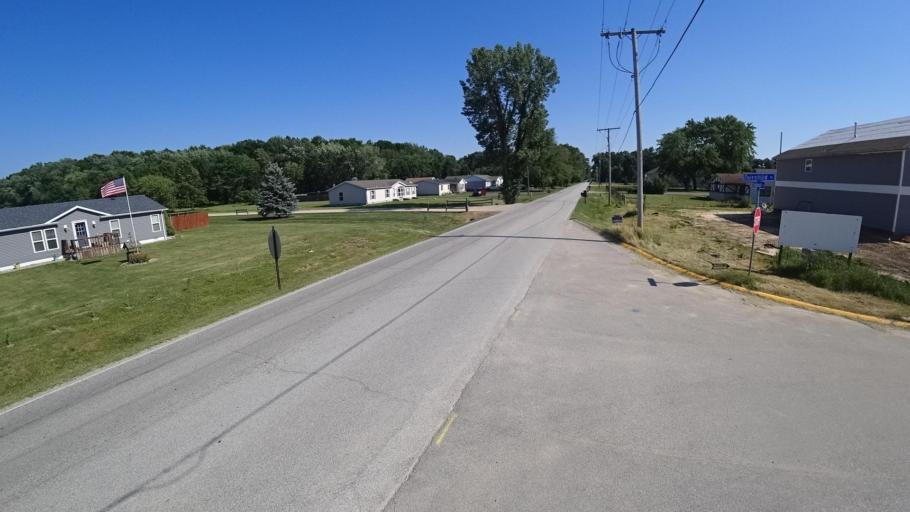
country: US
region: Indiana
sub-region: Porter County
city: Porter
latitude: 41.6038
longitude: -87.1056
